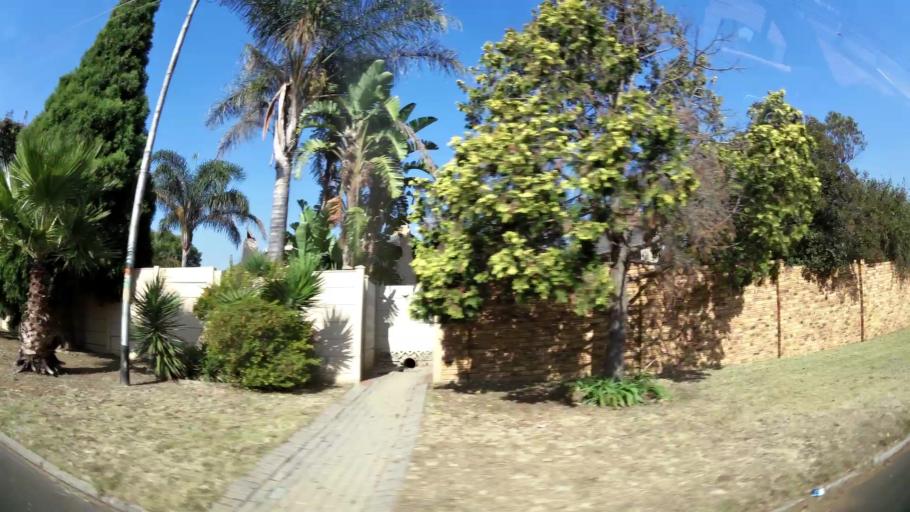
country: ZA
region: Gauteng
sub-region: West Rand District Municipality
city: Randfontein
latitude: -26.1592
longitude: 27.6946
